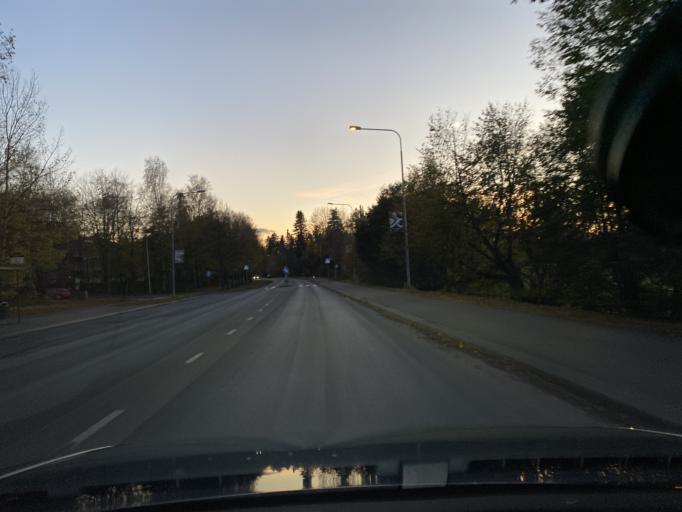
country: FI
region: Pirkanmaa
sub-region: Tampere
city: Tampere
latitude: 61.4733
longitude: 23.7593
